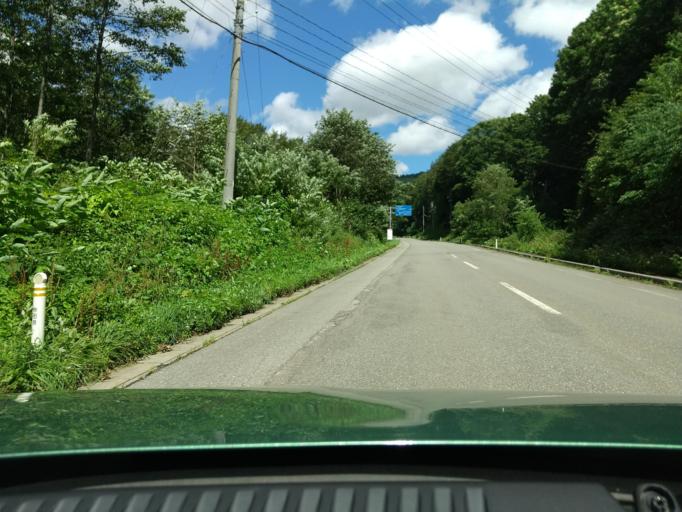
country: JP
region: Iwate
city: Shizukuishi
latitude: 39.7674
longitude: 140.7616
